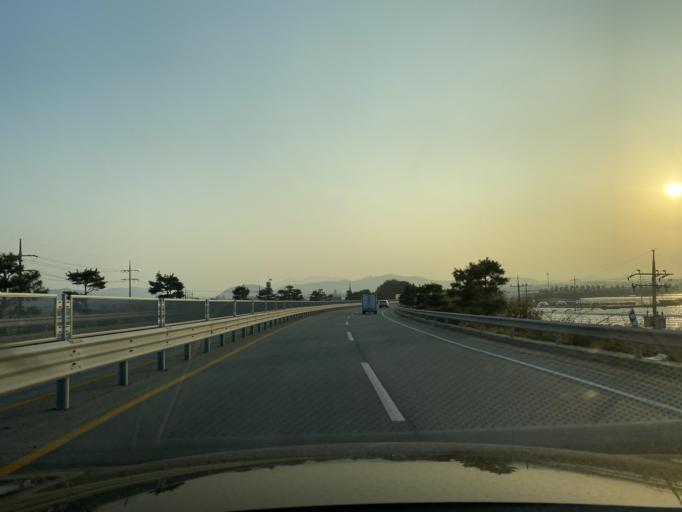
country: KR
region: Chungcheongnam-do
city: Yesan
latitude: 36.6998
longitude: 126.8203
